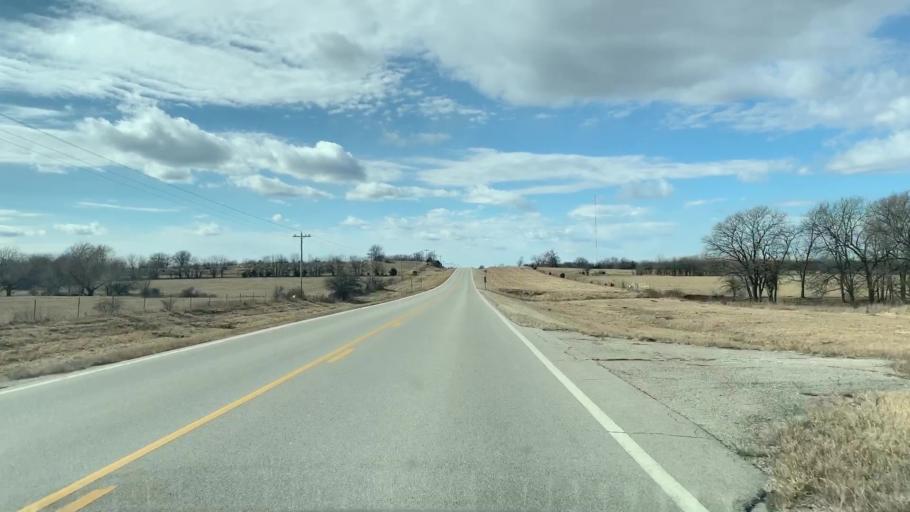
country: US
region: Kansas
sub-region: Neosho County
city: Erie
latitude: 37.5292
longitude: -95.3676
